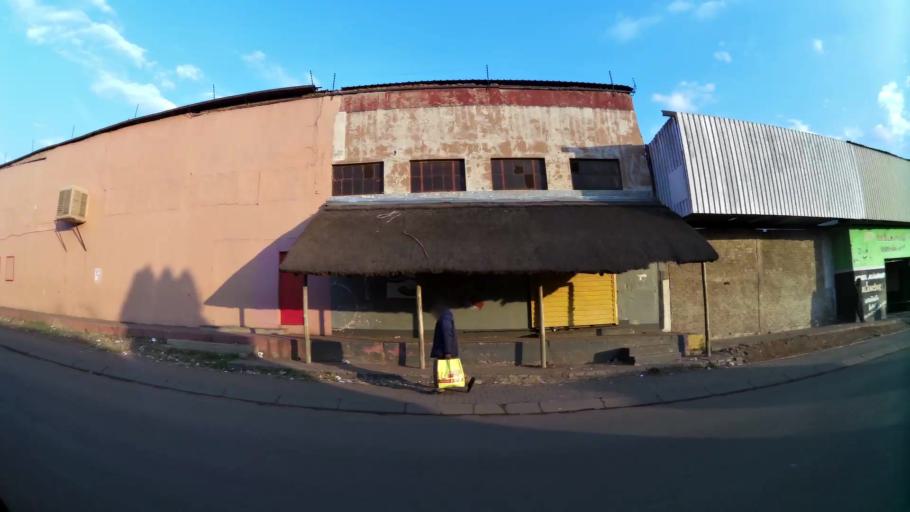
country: ZA
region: Gauteng
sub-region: City of Johannesburg Metropolitan Municipality
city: Orange Farm
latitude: -26.5342
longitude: 27.8495
